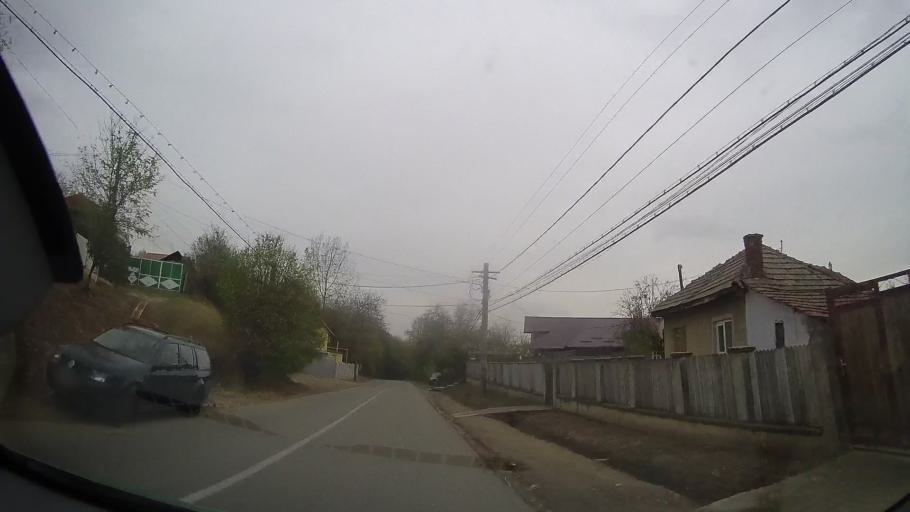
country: RO
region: Prahova
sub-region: Comuna Ceptura
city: Ceptura de Jos
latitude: 45.0248
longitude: 26.3240
